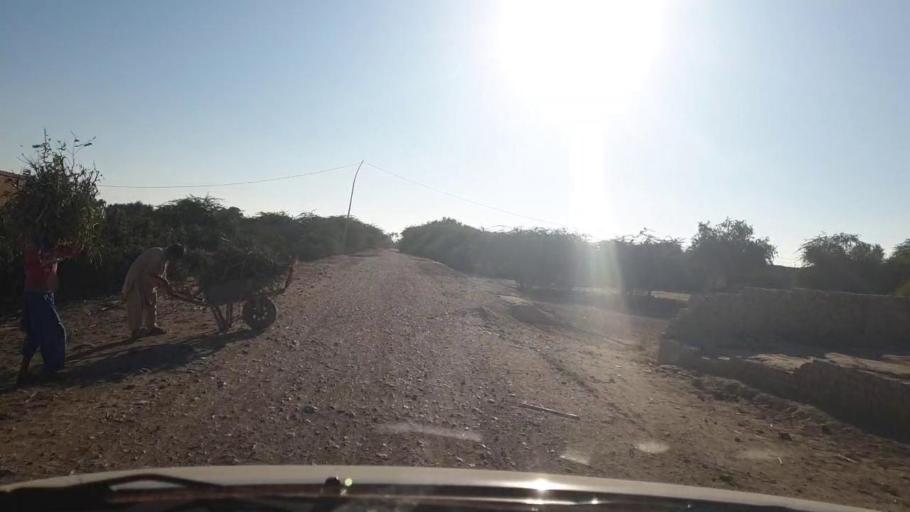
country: PK
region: Sindh
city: Johi
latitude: 26.7511
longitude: 67.4817
